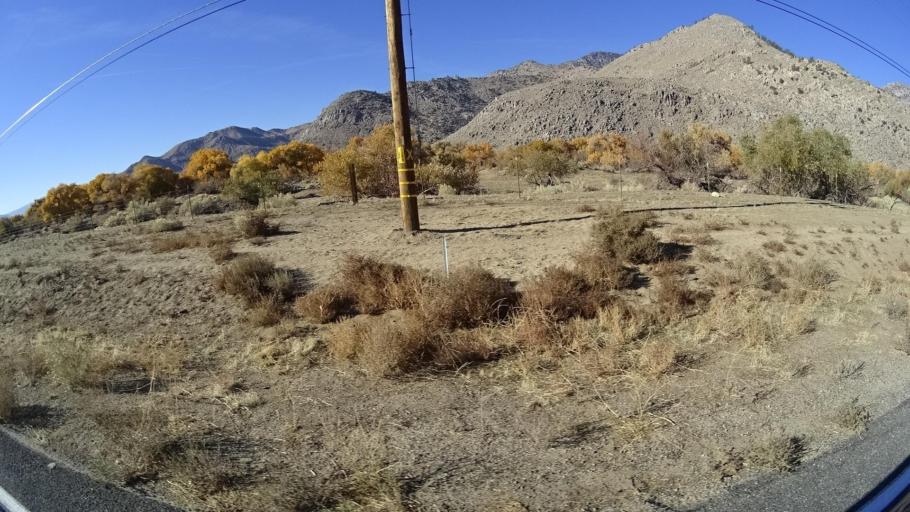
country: US
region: California
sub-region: Kern County
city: Weldon
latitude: 35.6888
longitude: -118.2348
